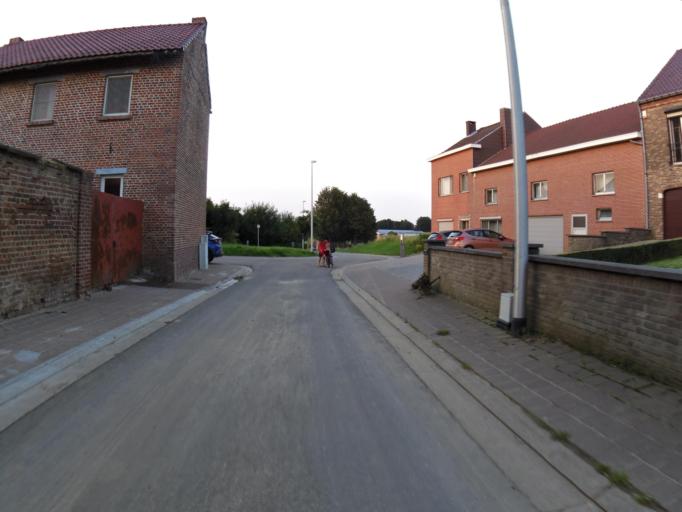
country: BE
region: Wallonia
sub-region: Province de Liege
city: Bassenge
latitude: 50.7675
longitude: 5.5577
